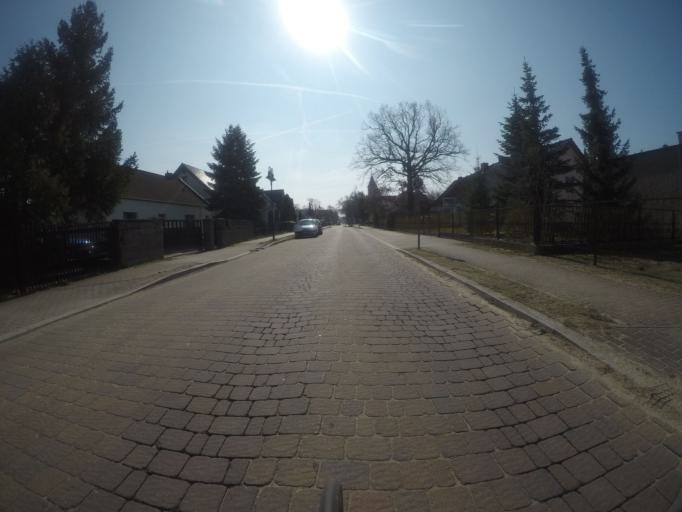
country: DE
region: Brandenburg
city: Erkner
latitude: 52.3957
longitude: 13.7128
